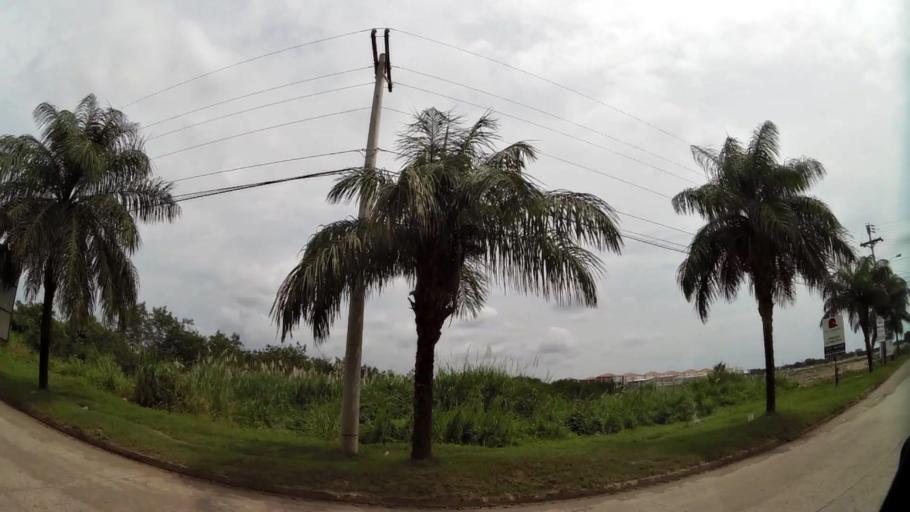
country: PA
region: Panama
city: San Miguelito
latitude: 9.0333
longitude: -79.4217
